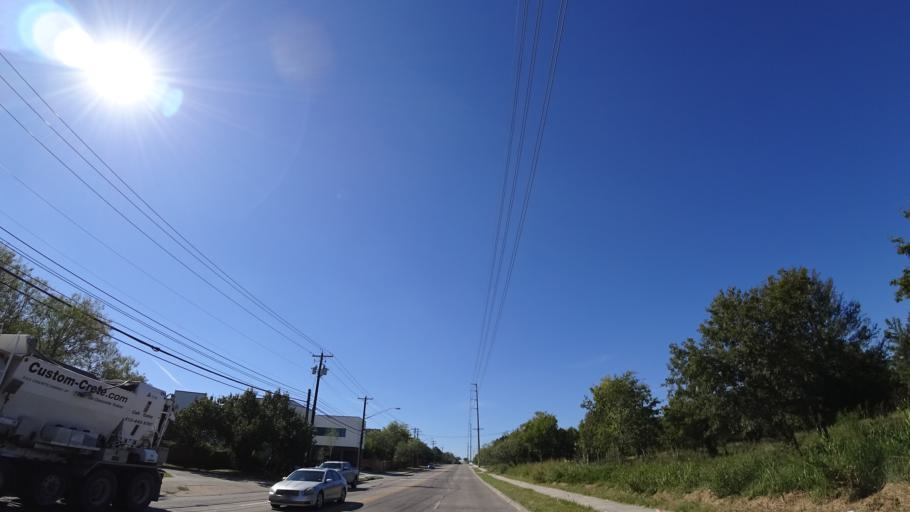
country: US
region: Texas
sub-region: Travis County
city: Austin
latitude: 30.2244
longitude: -97.7038
